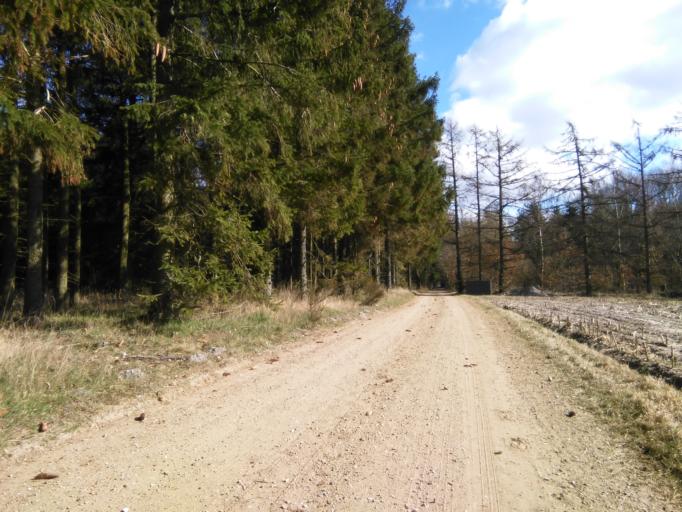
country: DK
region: Central Jutland
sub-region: Skanderborg Kommune
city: Ry
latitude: 56.0524
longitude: 9.7154
